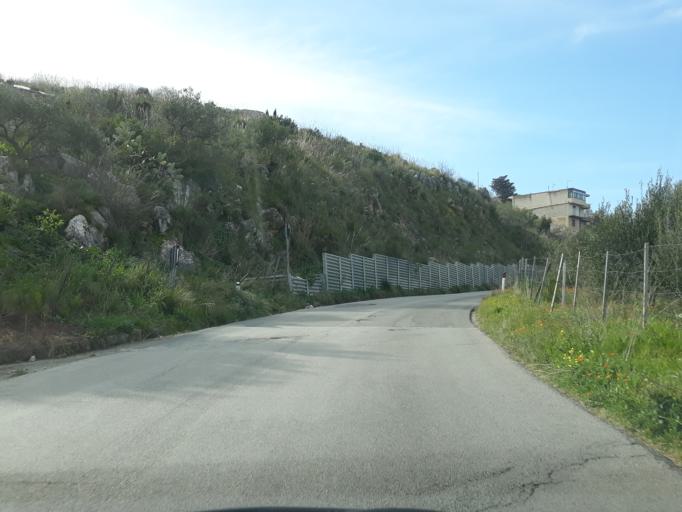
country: IT
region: Sicily
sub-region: Palermo
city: Altofonte
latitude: 38.0405
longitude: 13.3106
